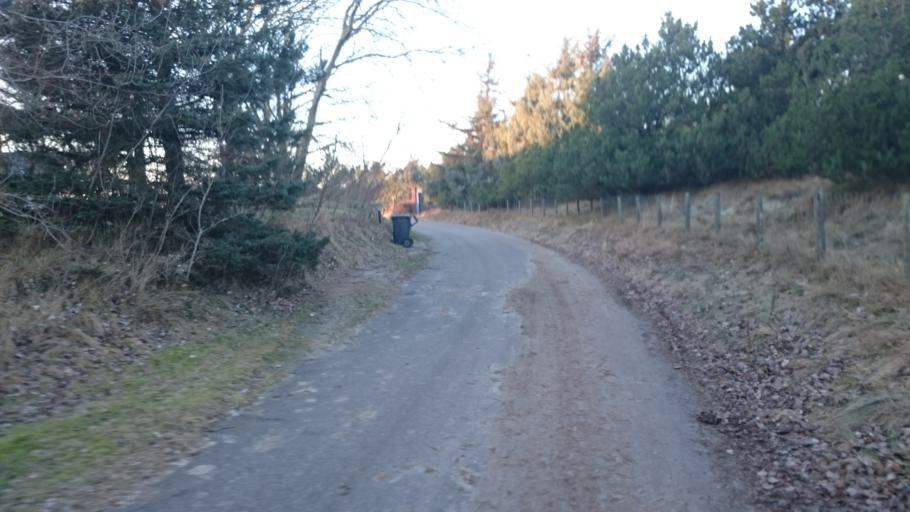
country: DK
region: South Denmark
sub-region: Fano Kommune
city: Nordby
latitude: 55.4512
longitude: 8.3998
